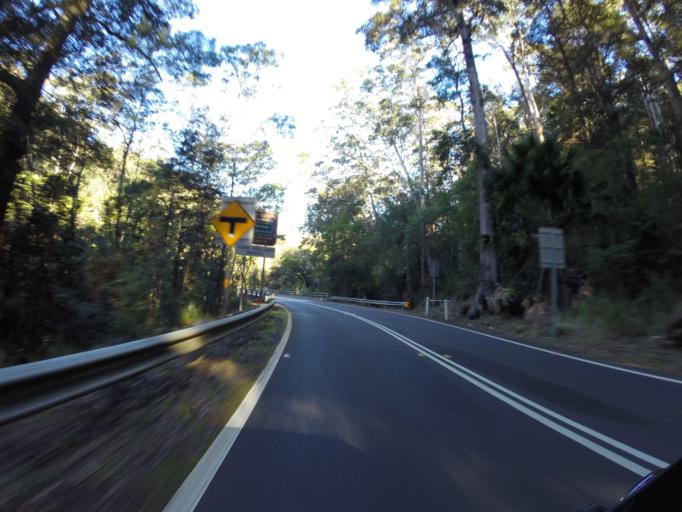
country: AU
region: New South Wales
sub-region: Wollongong
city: Helensburgh
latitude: -34.1515
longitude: 151.0282
